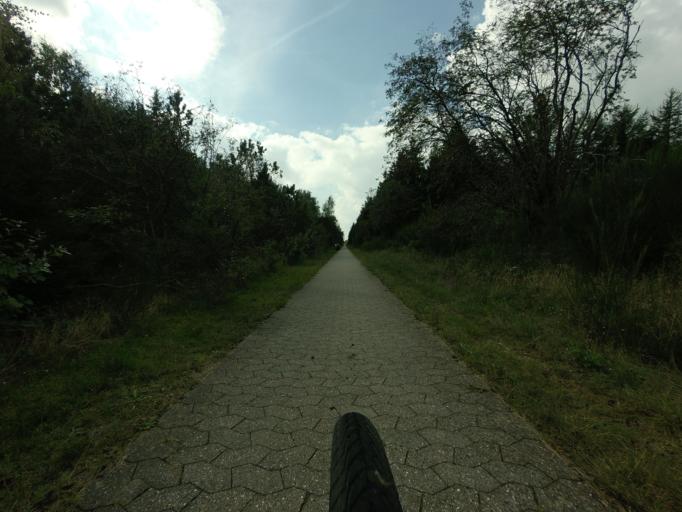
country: DK
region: Central Jutland
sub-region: Viborg Kommune
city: Karup
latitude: 56.3195
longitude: 9.2051
